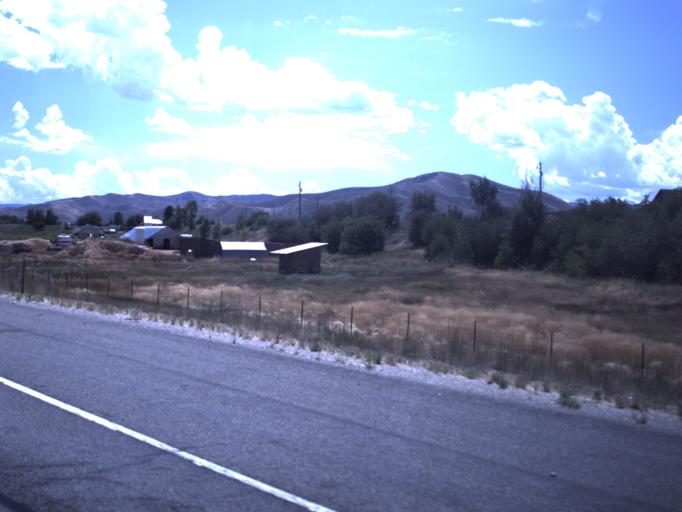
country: US
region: Utah
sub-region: Morgan County
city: Morgan
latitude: 41.0409
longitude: -111.5185
